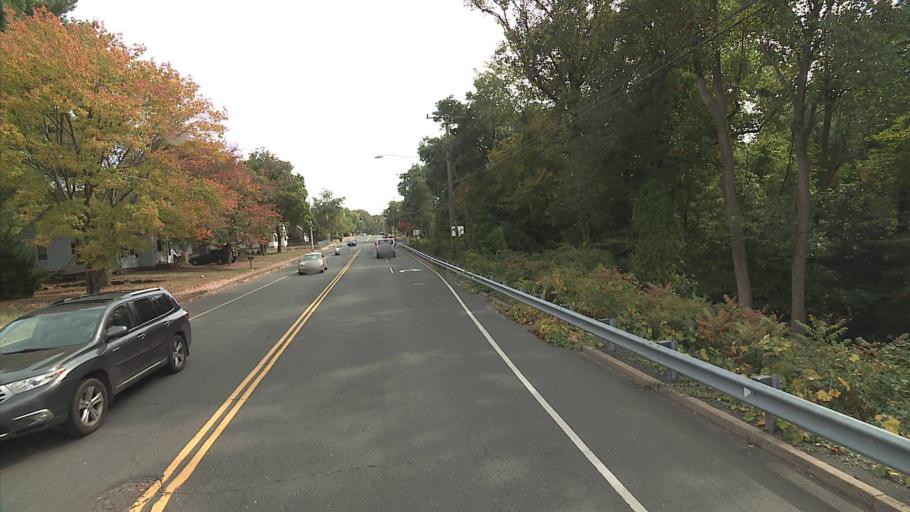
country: US
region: Connecticut
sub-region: Hartford County
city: Manchester
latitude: 41.7800
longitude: -72.5587
